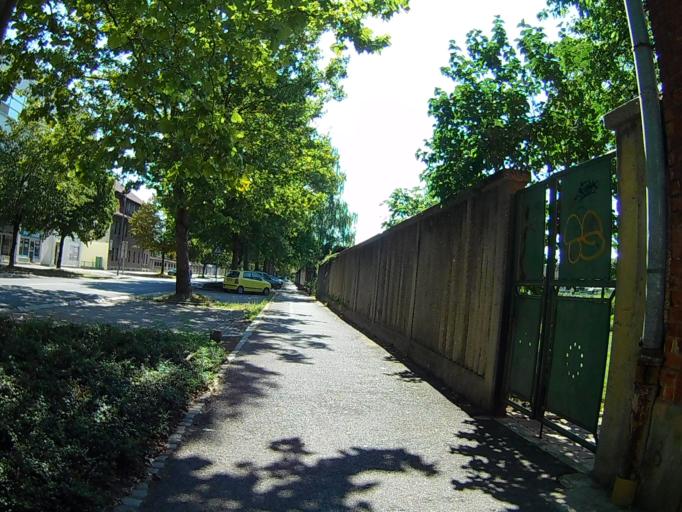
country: SI
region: Maribor
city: Maribor
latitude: 46.5544
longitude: 15.6358
